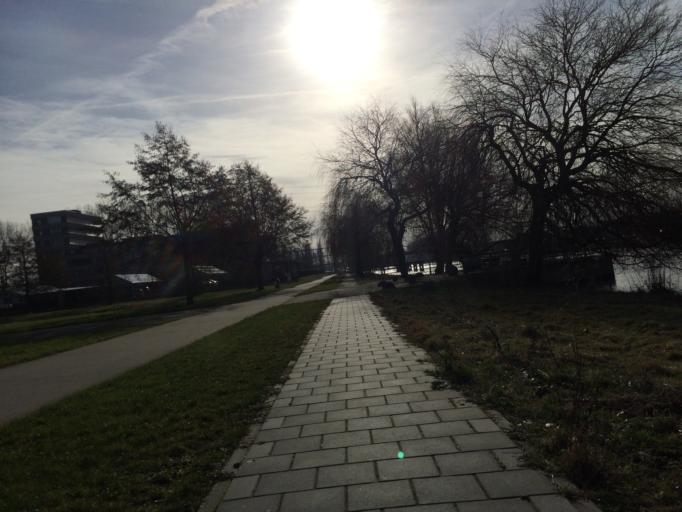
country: NL
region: Flevoland
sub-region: Gemeente Almere
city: Almere Stad
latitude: 52.3761
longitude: 5.2537
